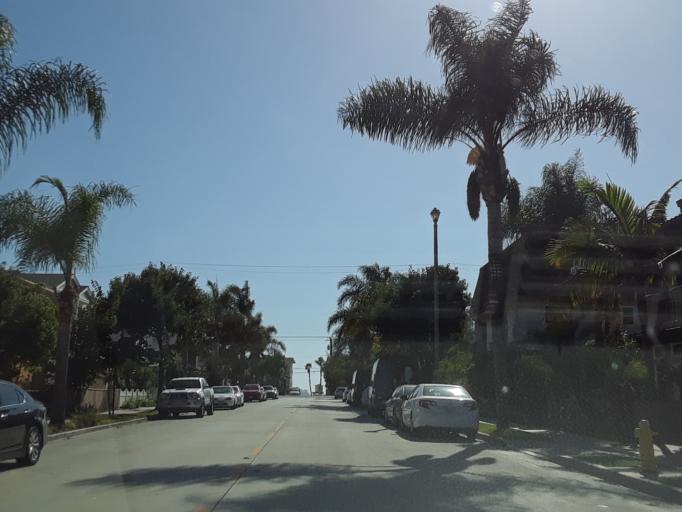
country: US
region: California
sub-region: Orange County
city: Seal Beach
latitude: 33.7396
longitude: -118.1025
